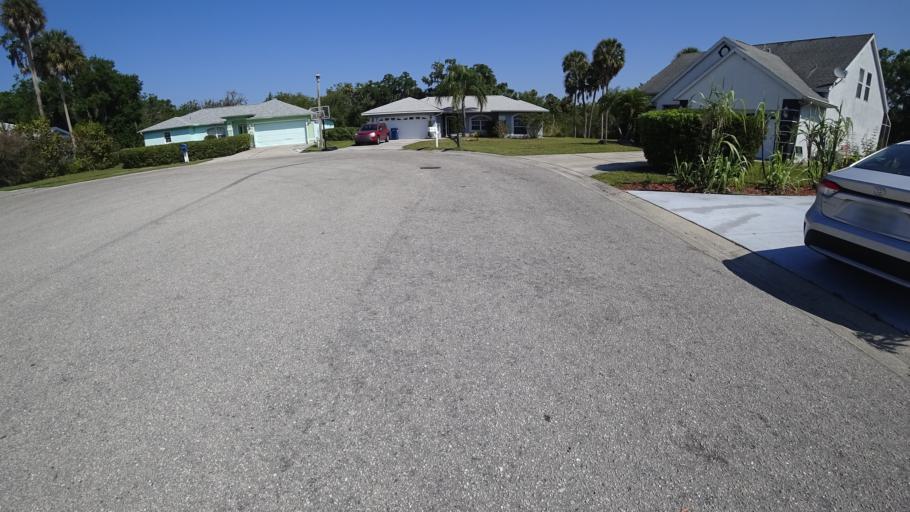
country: US
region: Florida
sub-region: Manatee County
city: Samoset
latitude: 27.4675
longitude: -82.5224
